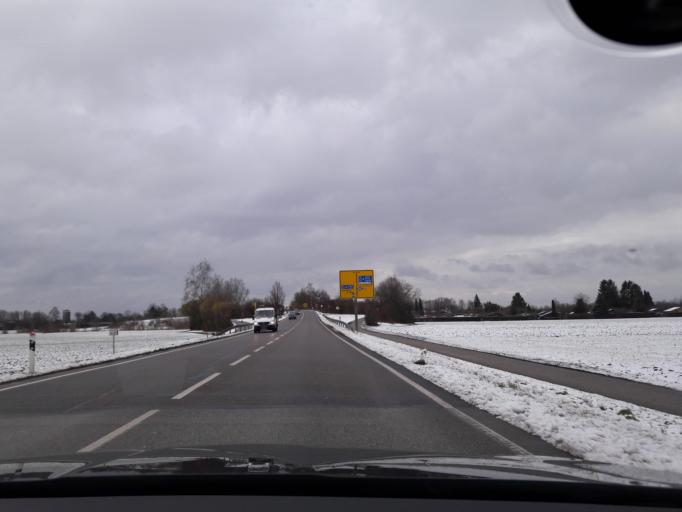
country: DE
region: Bavaria
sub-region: Upper Bavaria
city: Karlsfeld
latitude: 48.2510
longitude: 11.4735
